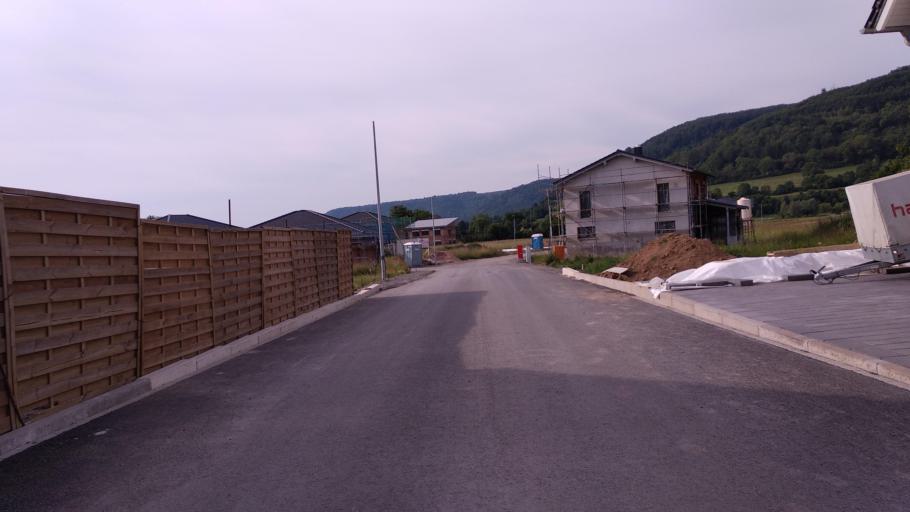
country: DE
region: North Rhine-Westphalia
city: Beverungen
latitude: 51.6609
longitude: 9.3671
